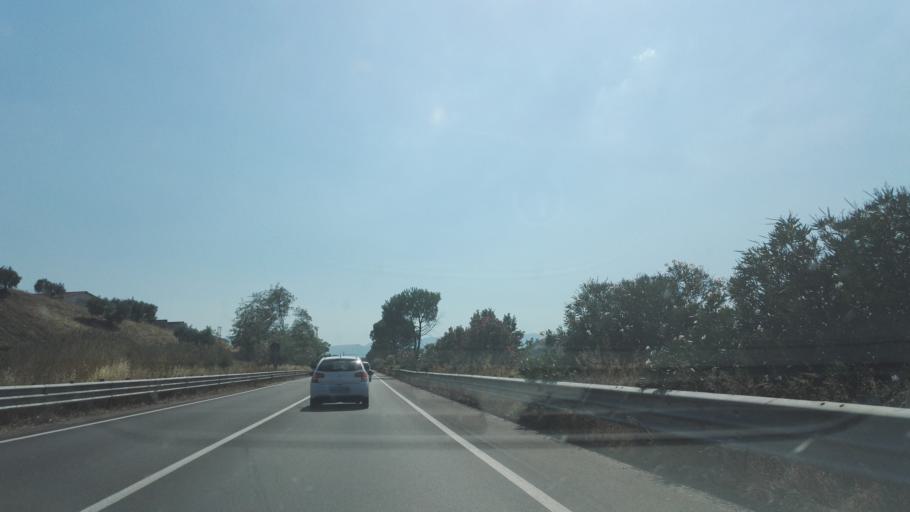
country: IT
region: Calabria
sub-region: Provincia di Cosenza
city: San Lorenzo del Vallo
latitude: 39.6624
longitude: 16.2648
